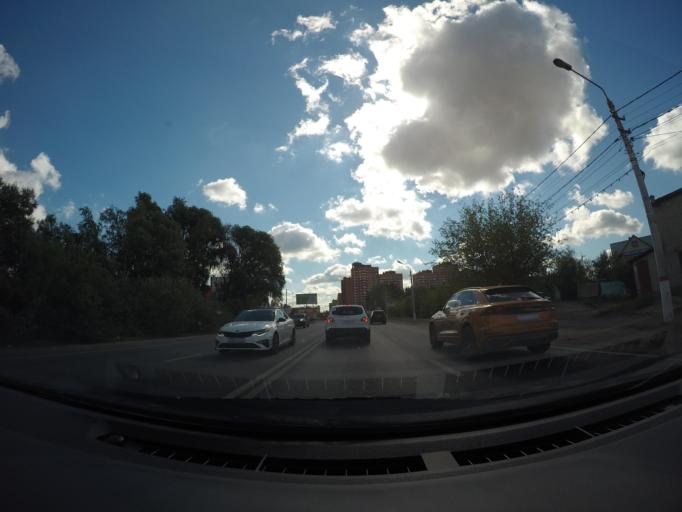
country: RU
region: Moskovskaya
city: Ramenskoye
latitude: 55.5834
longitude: 38.2407
